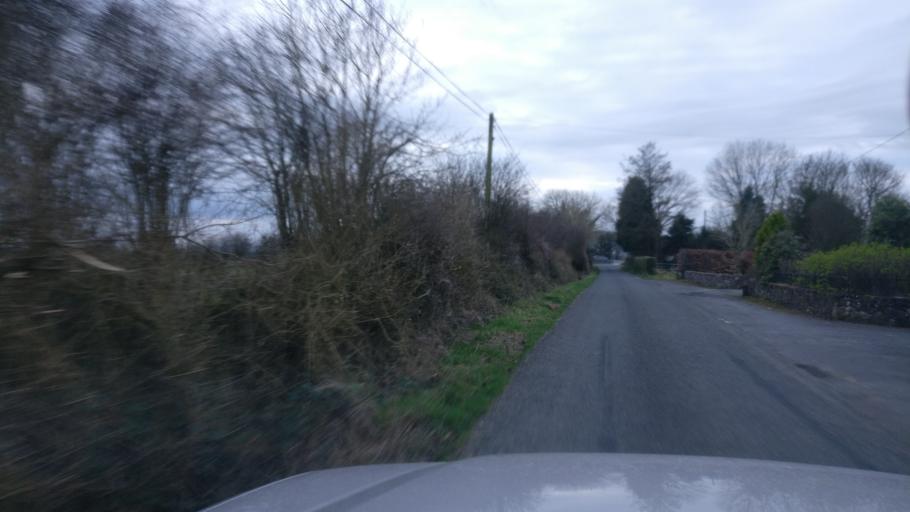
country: IE
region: Connaught
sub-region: County Galway
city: Loughrea
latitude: 53.2526
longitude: -8.5115
